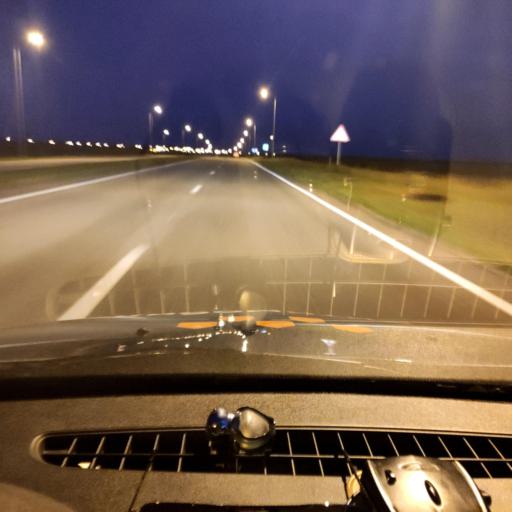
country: RU
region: Belgorod
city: Skorodnoye
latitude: 51.0672
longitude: 37.2039
